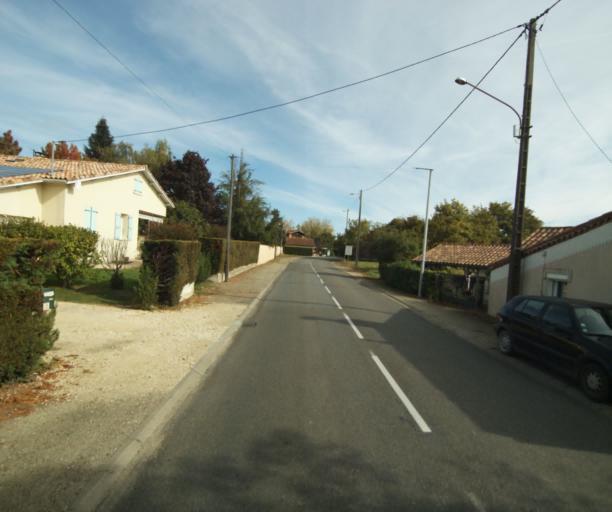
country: FR
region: Midi-Pyrenees
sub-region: Departement du Gers
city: Eauze
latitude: 43.8853
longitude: 0.1356
